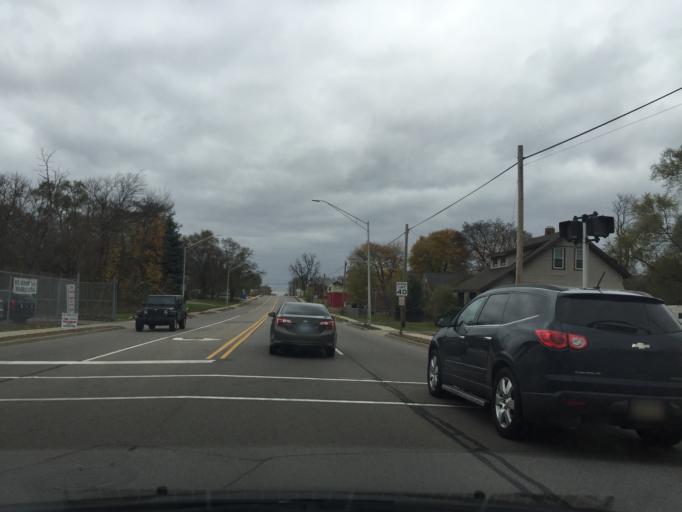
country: US
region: Michigan
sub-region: Oakland County
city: Pontiac
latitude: 42.6465
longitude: -83.3015
